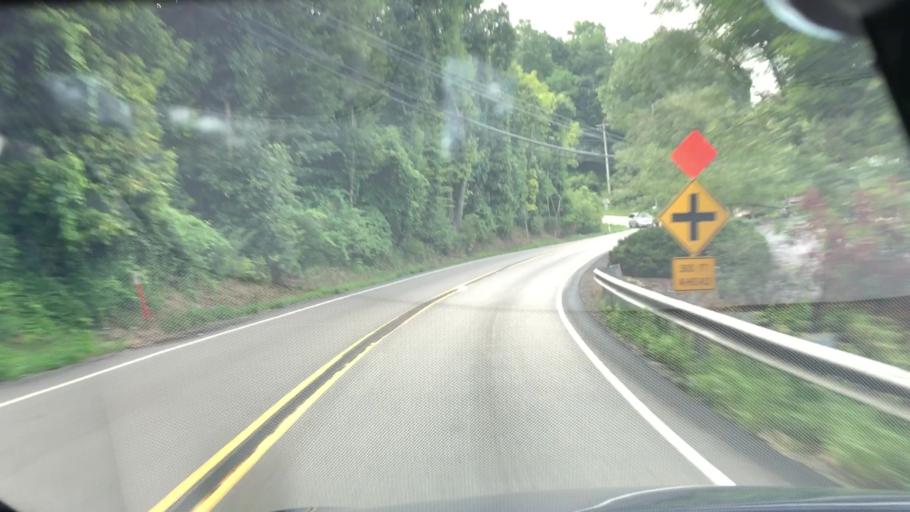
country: US
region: Pennsylvania
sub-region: Washington County
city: Thompsonville
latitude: 40.2874
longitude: -80.0995
